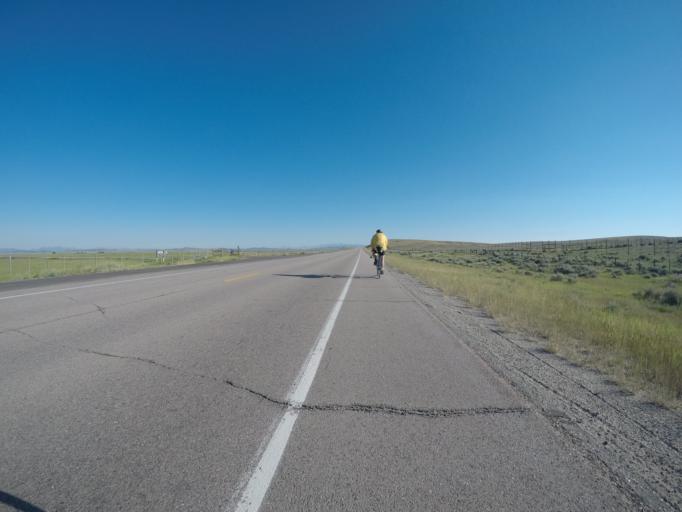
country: US
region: Wyoming
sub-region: Sublette County
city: Pinedale
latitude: 42.9378
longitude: -110.0820
